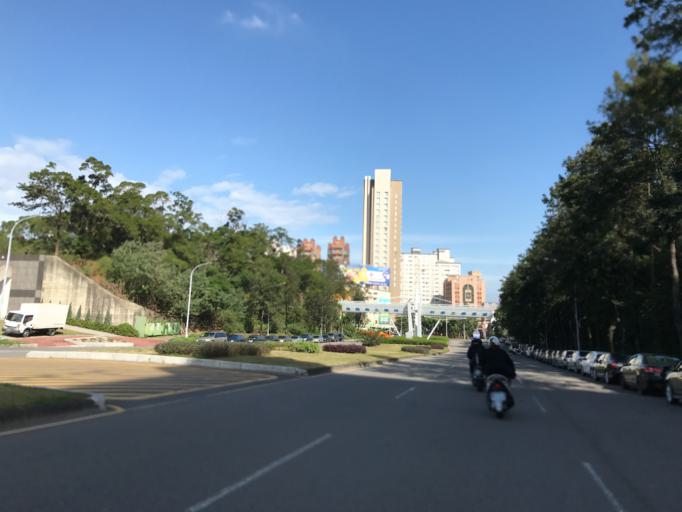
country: TW
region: Taiwan
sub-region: Hsinchu
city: Hsinchu
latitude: 24.7789
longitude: 121.0195
